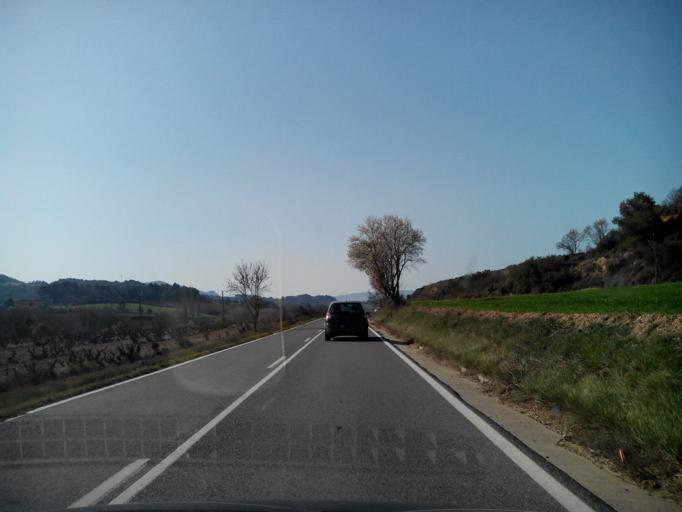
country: ES
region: Catalonia
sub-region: Provincia de Tarragona
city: Fores
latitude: 41.4596
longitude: 1.2659
